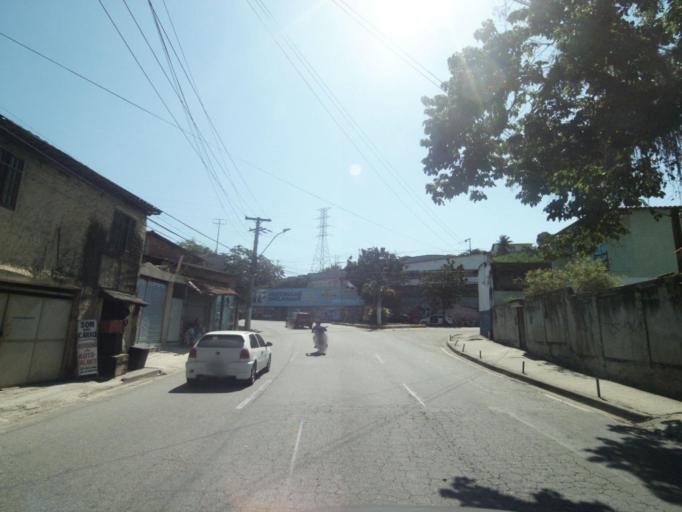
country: BR
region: Rio de Janeiro
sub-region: Niteroi
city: Niteroi
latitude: -22.9057
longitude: -43.0648
